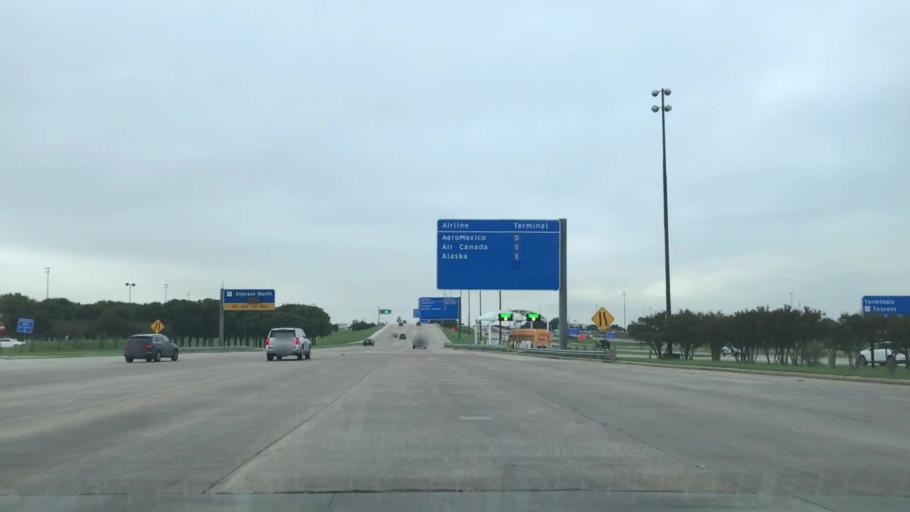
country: US
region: Texas
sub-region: Tarrant County
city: Grapevine
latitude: 32.9221
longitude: -97.0410
